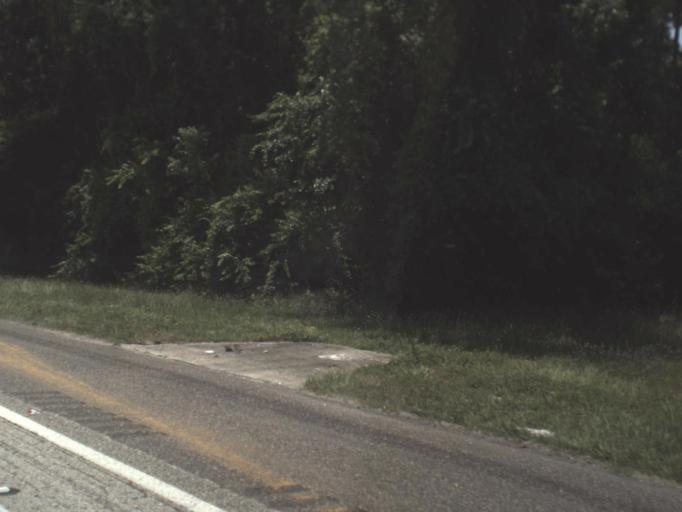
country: US
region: Florida
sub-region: Saint Johns County
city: Fruit Cove
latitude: 30.1279
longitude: -81.5275
